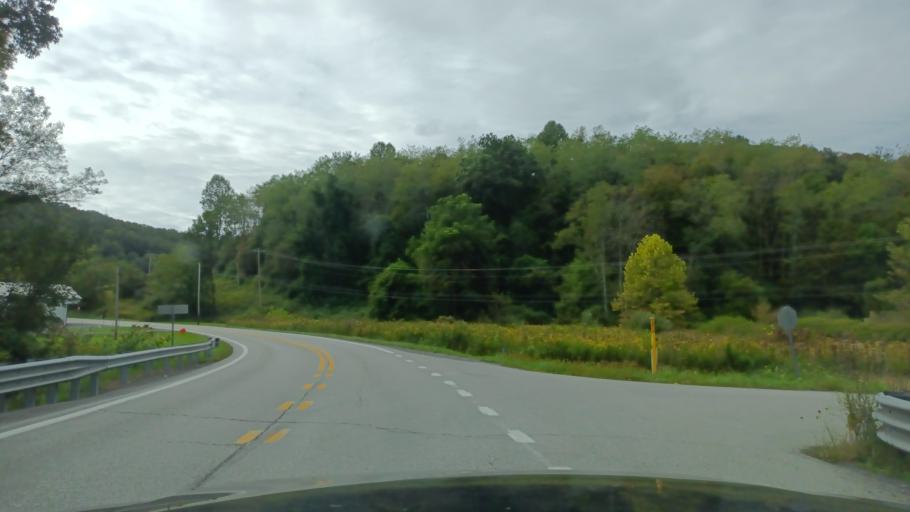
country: US
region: West Virginia
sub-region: Taylor County
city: Grafton
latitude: 39.3251
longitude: -80.1153
